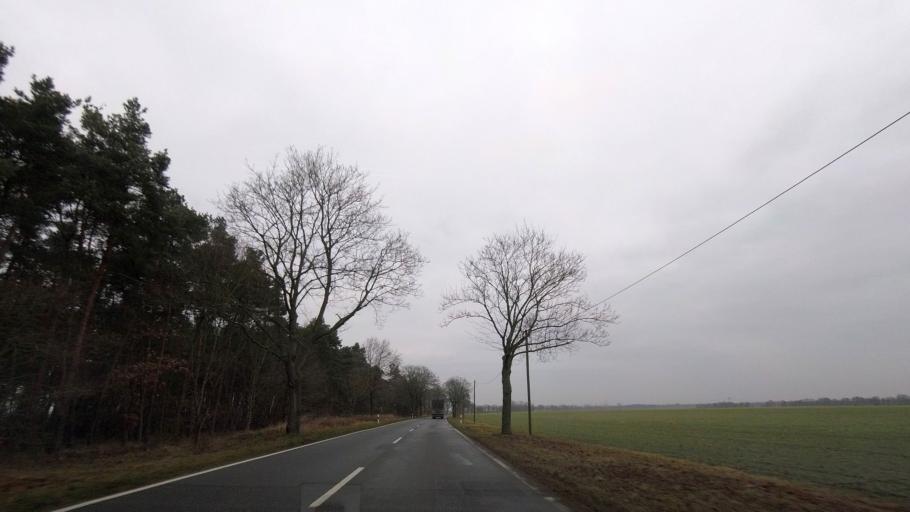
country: DE
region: Brandenburg
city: Treuenbrietzen
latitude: 52.0964
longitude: 12.9477
